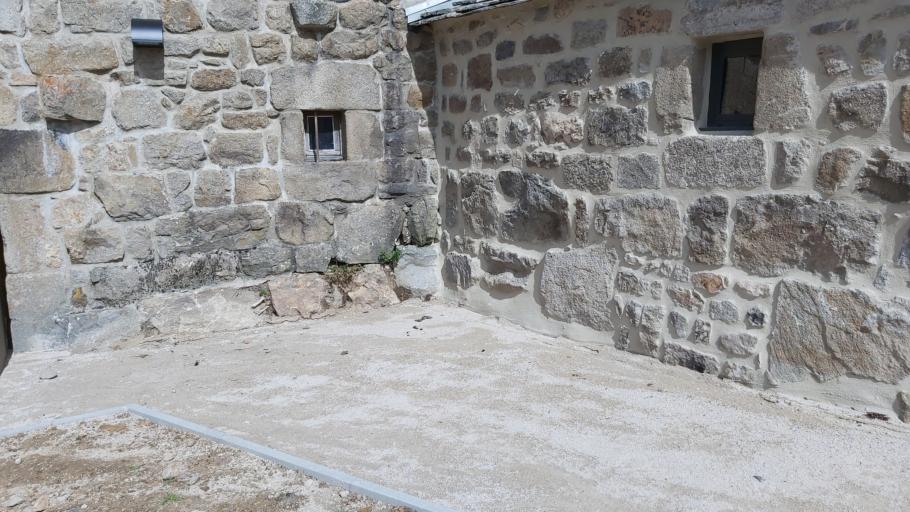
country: FR
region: Rhone-Alpes
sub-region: Departement de l'Ardeche
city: Saint-Agreve
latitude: 45.0515
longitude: 4.3952
